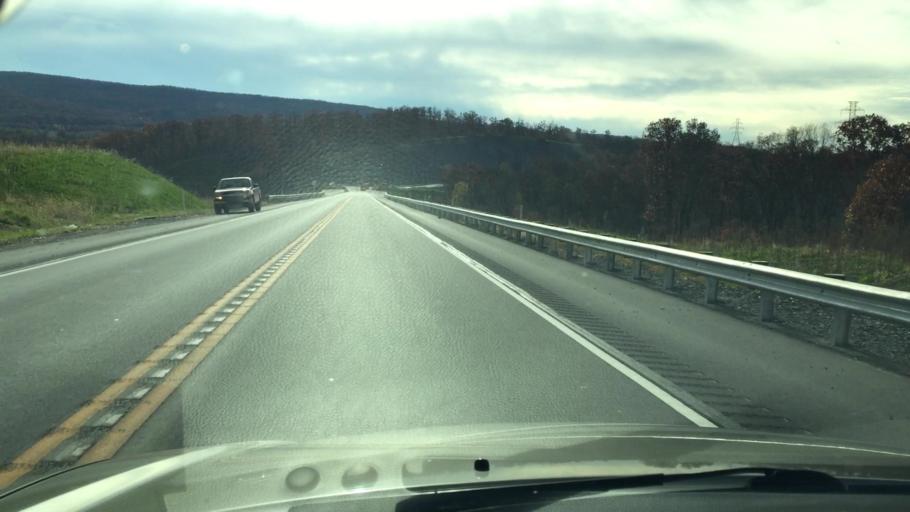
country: US
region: Pennsylvania
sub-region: Luzerne County
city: Nanticoke
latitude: 41.2013
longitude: -75.9629
